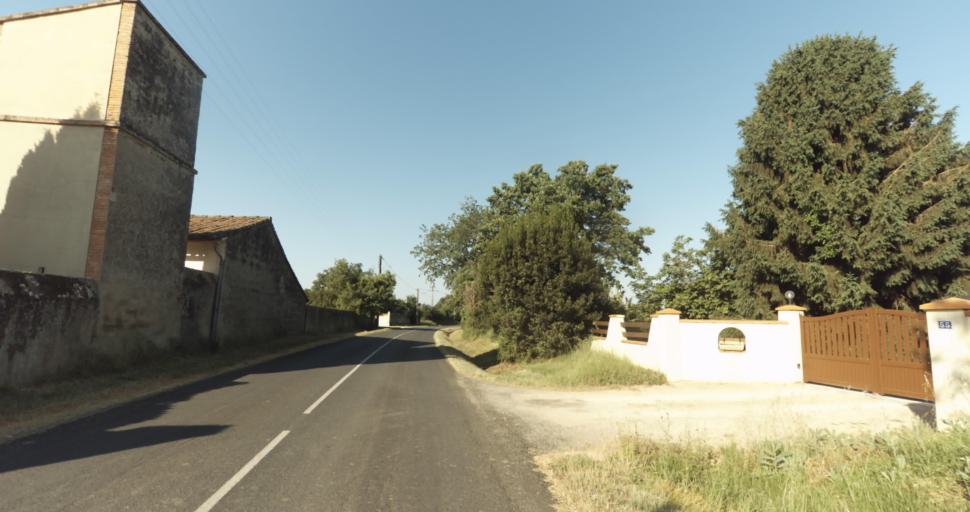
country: FR
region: Midi-Pyrenees
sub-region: Departement de la Haute-Garonne
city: Fontenilles
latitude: 43.5601
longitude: 1.2020
